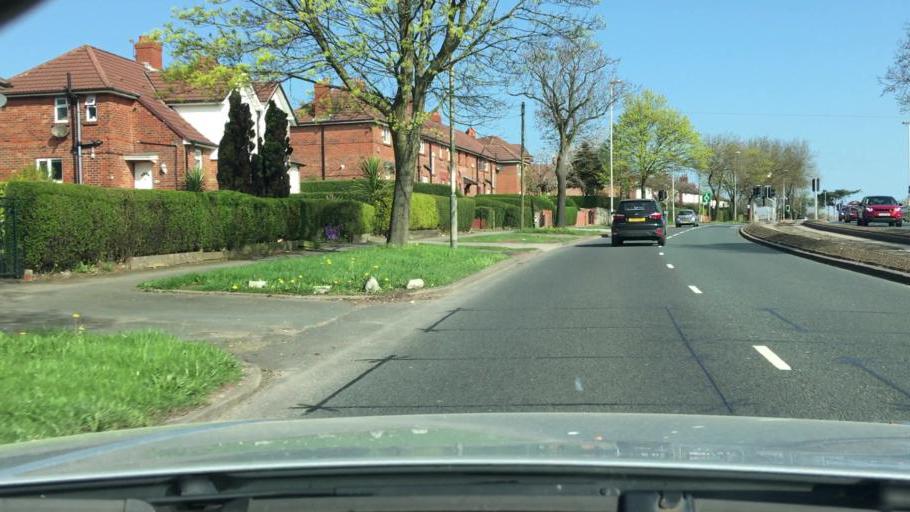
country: GB
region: England
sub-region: City and Borough of Leeds
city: Chapel Allerton
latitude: 53.8265
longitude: -1.5473
